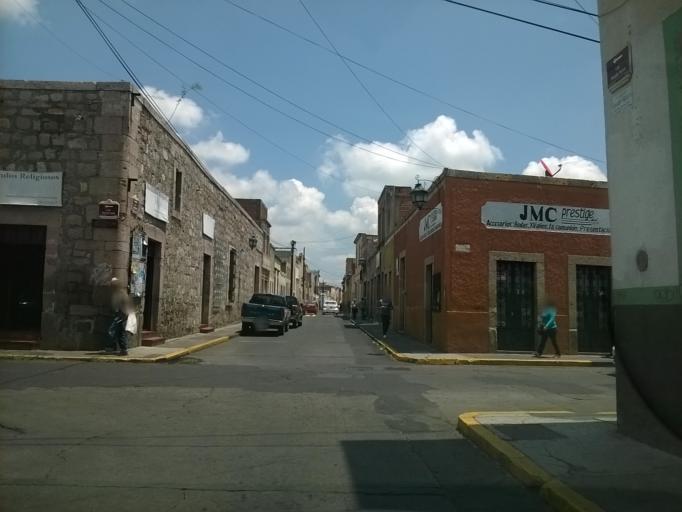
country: MX
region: Michoacan
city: Morelia
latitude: 19.7056
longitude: -101.1855
